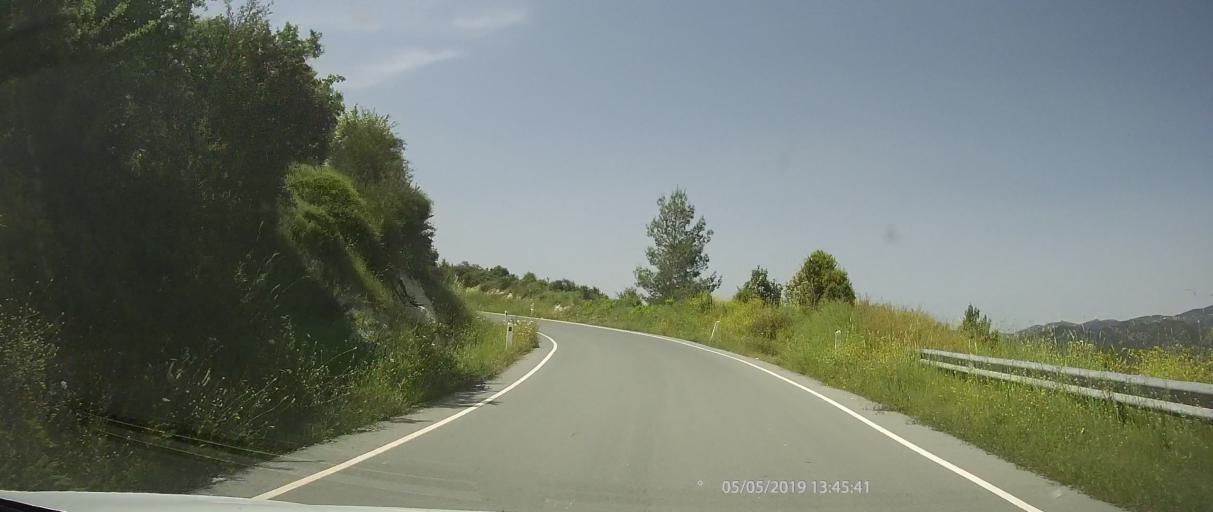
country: CY
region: Limassol
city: Pachna
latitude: 34.8706
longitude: 32.7798
